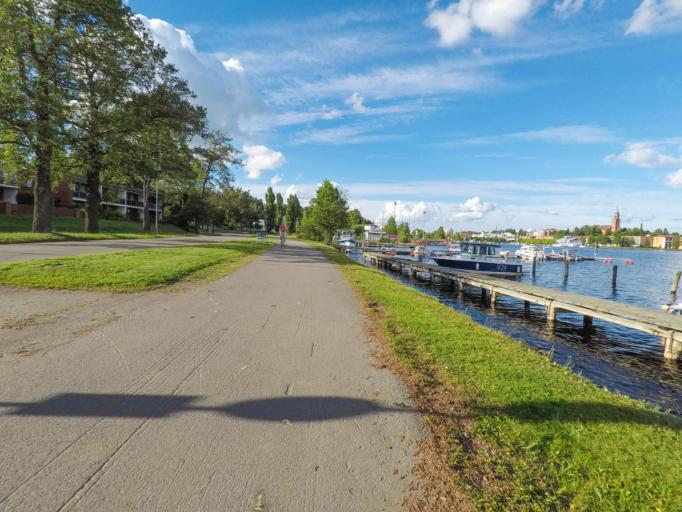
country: FI
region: Southern Savonia
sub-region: Savonlinna
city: Savonlinna
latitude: 61.8648
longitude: 28.8669
